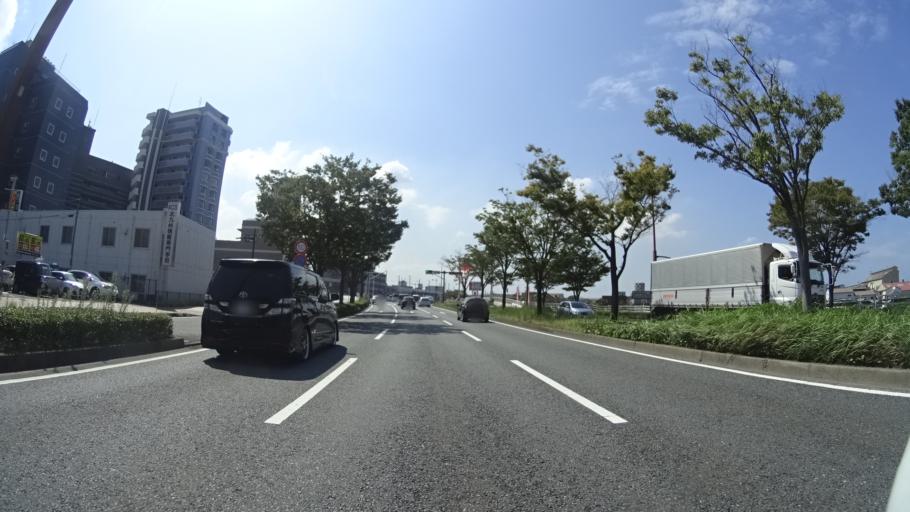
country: JP
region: Fukuoka
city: Kitakyushu
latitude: 33.8896
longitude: 130.8796
